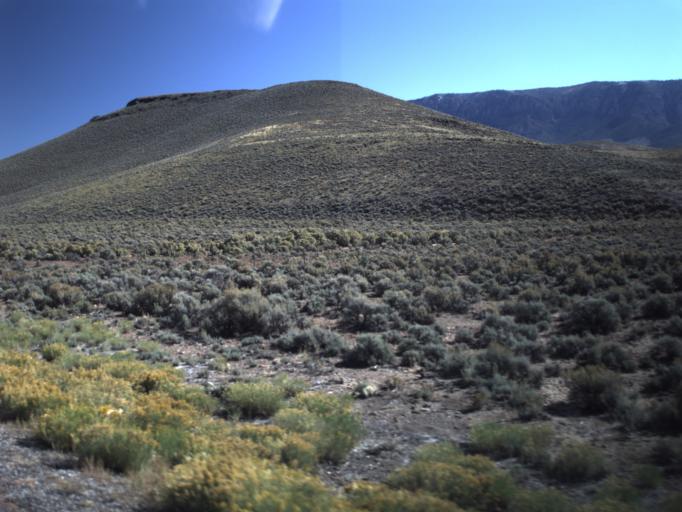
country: US
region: Utah
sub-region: Piute County
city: Junction
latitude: 38.2723
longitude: -111.9863
